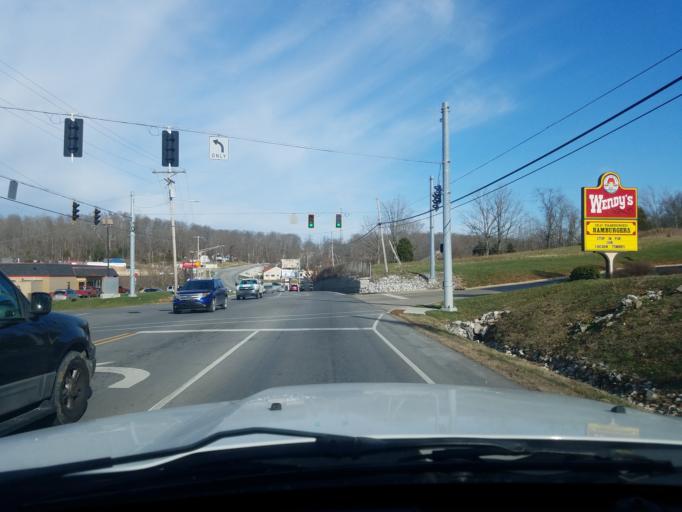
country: US
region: Indiana
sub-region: Orange County
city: Paoli
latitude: 38.5649
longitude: -86.4655
